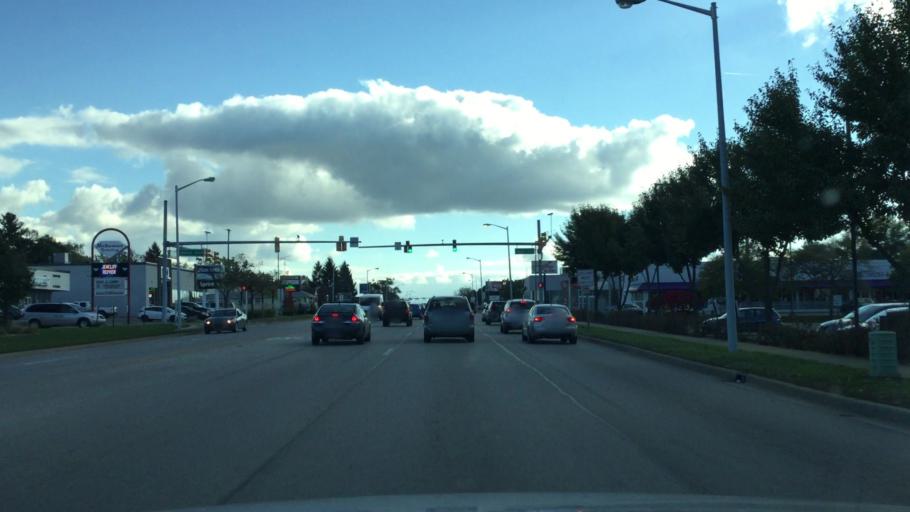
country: US
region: Michigan
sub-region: Kalamazoo County
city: Portage
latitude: 42.2344
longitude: -85.5896
